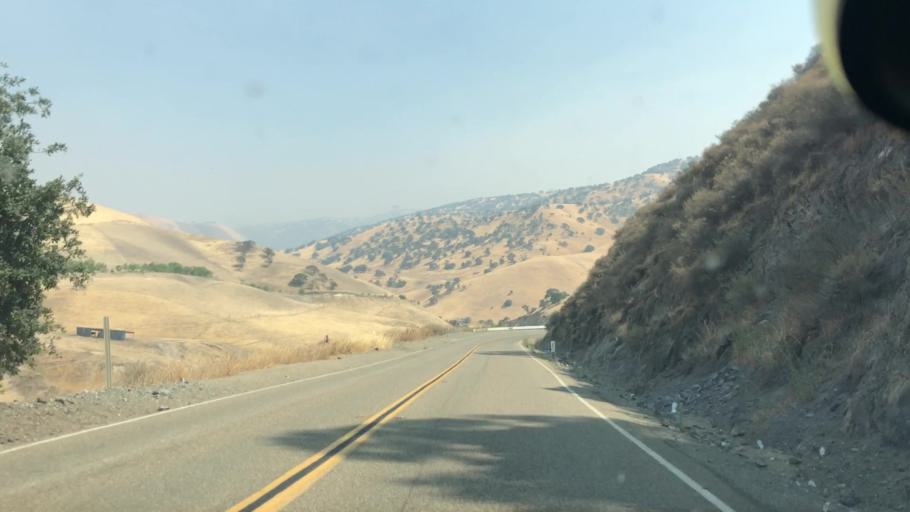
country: US
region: California
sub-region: San Joaquin County
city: Mountain House
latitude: 37.6482
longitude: -121.5989
